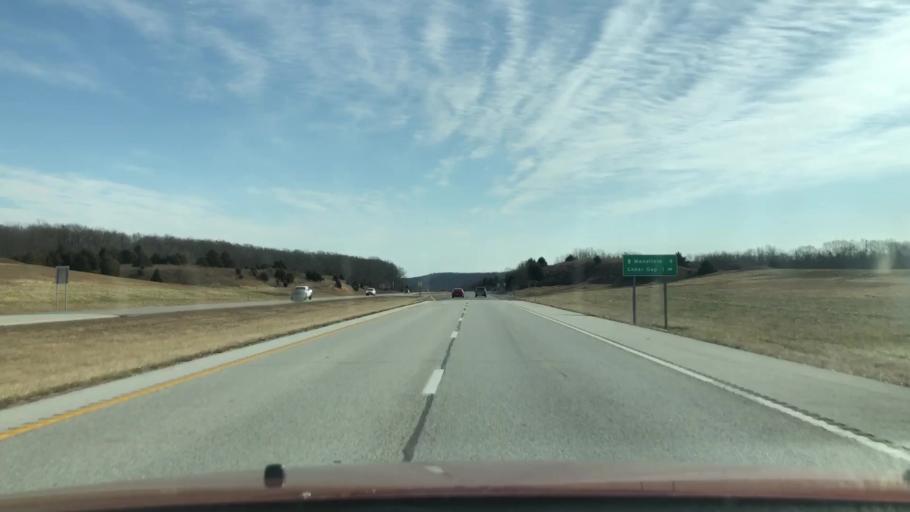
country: US
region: Missouri
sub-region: Wright County
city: Mansfield
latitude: 37.1159
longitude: -92.6769
